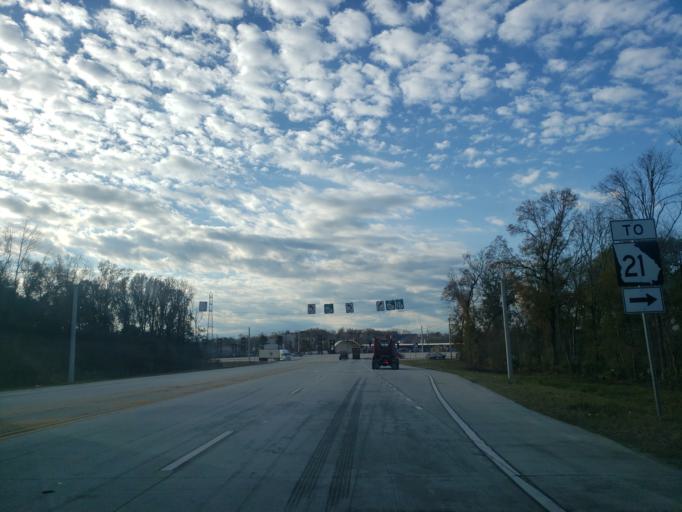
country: US
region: Georgia
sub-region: Chatham County
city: Garden City
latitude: 32.1277
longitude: -81.1641
